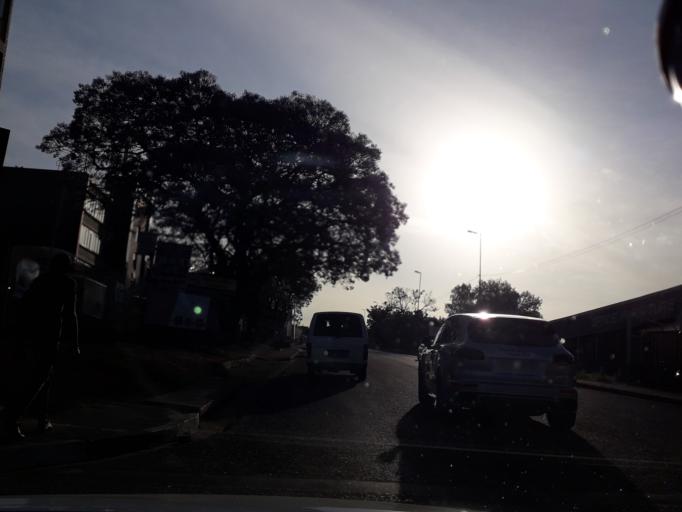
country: ZA
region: Gauteng
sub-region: City of Johannesburg Metropolitan Municipality
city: Johannesburg
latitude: -26.0814
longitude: 27.9860
